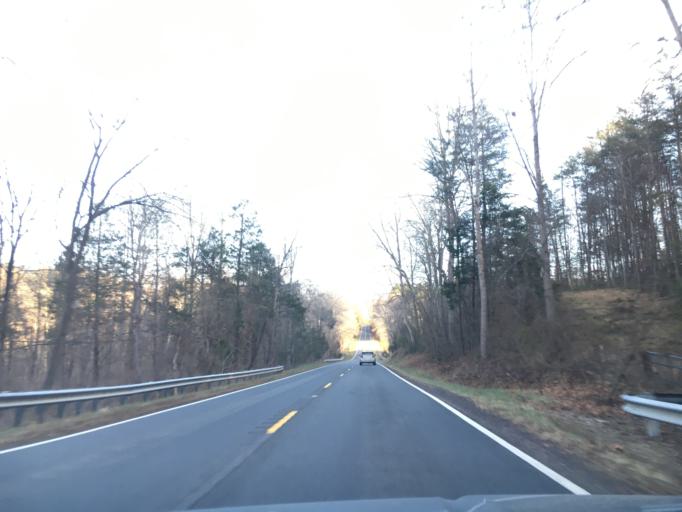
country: US
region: Virginia
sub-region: Culpeper County
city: Merrimac
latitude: 38.5534
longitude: -78.1483
